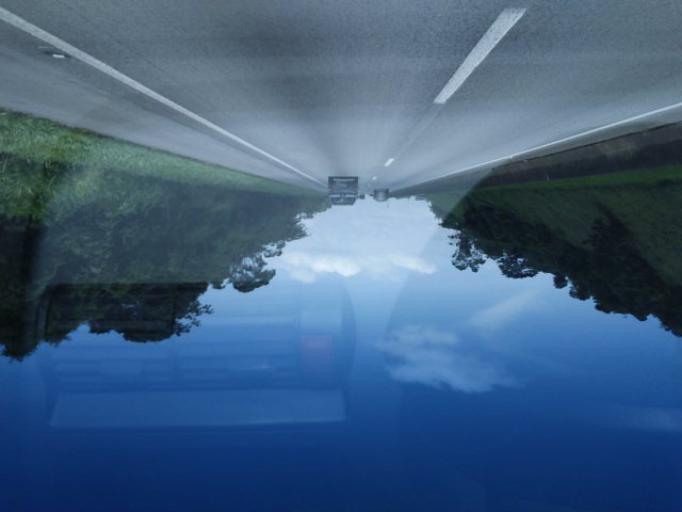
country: BR
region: Sao Paulo
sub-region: Registro
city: Registro
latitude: -24.4396
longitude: -47.7965
